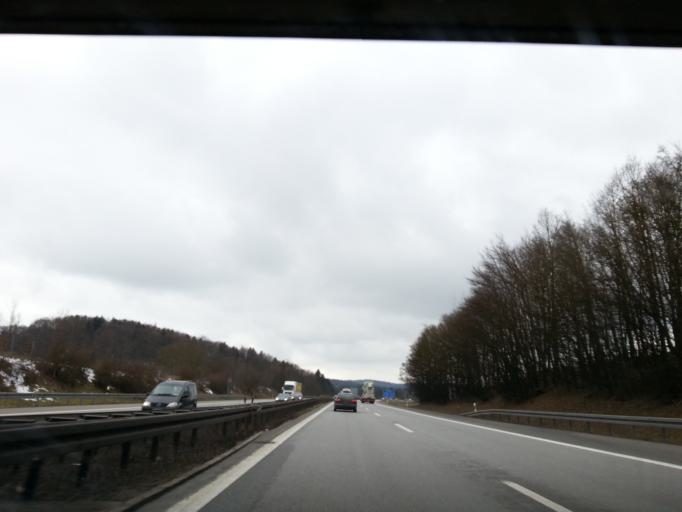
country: DE
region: Bavaria
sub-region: Upper Palatinate
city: Hohenfels
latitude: 49.1478
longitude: 11.8517
